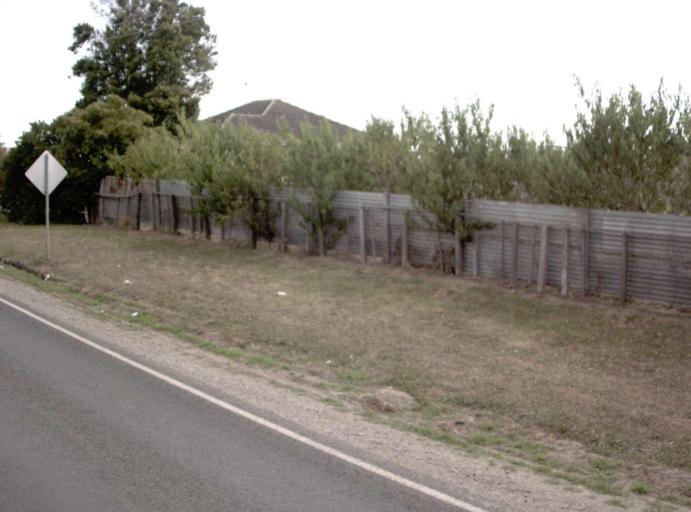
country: AU
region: Victoria
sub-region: Casey
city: Junction Village
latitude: -38.1287
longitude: 145.3252
